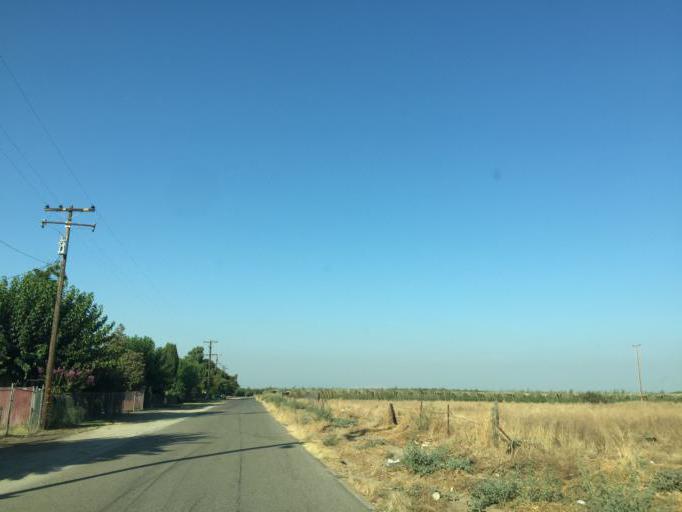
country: US
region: California
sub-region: Tulare County
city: London
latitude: 36.4535
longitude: -119.4844
